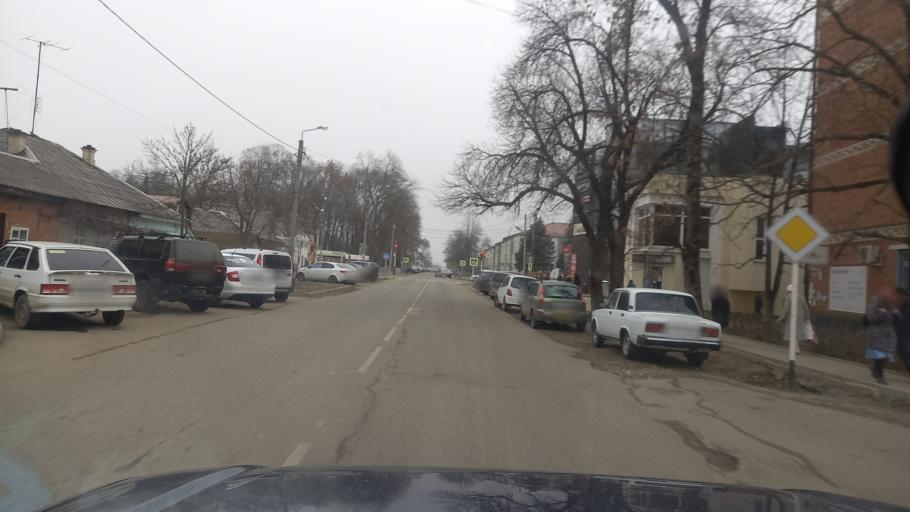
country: RU
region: Krasnodarskiy
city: Apsheronsk
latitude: 44.4634
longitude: 39.7407
